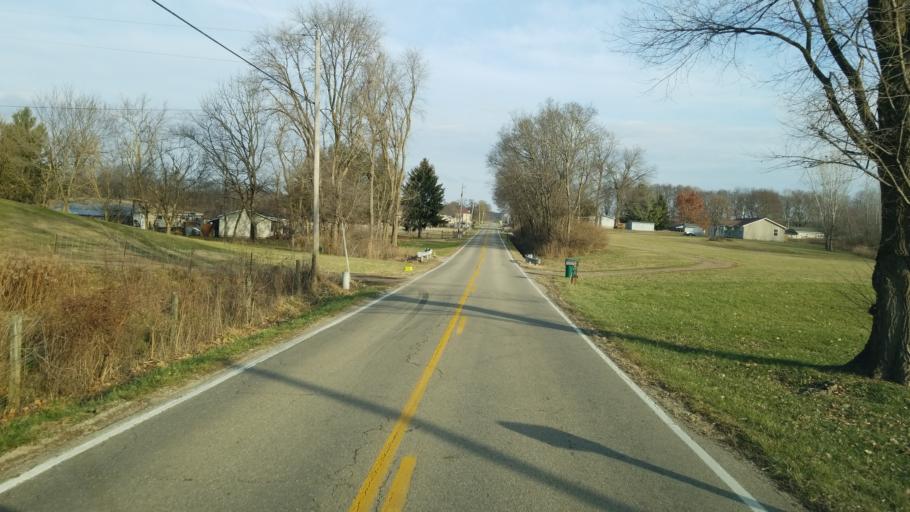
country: US
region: Ohio
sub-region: Ross County
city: Kingston
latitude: 39.4207
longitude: -82.9398
